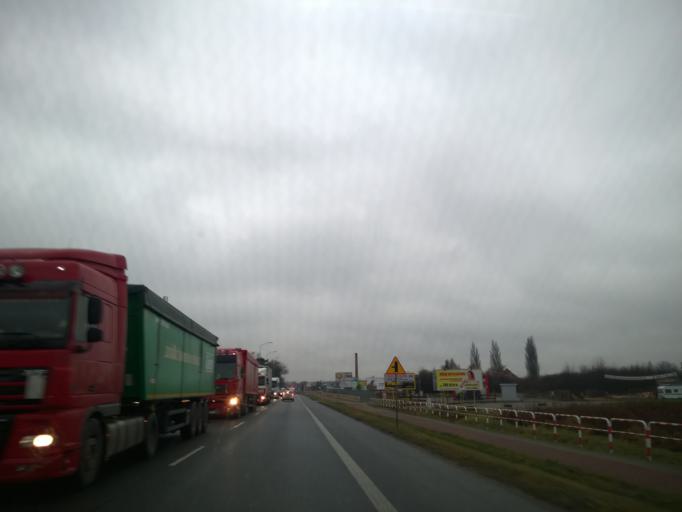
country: PL
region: Lower Silesian Voivodeship
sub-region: Powiat trzebnicki
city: Psary
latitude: 51.1927
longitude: 17.0316
